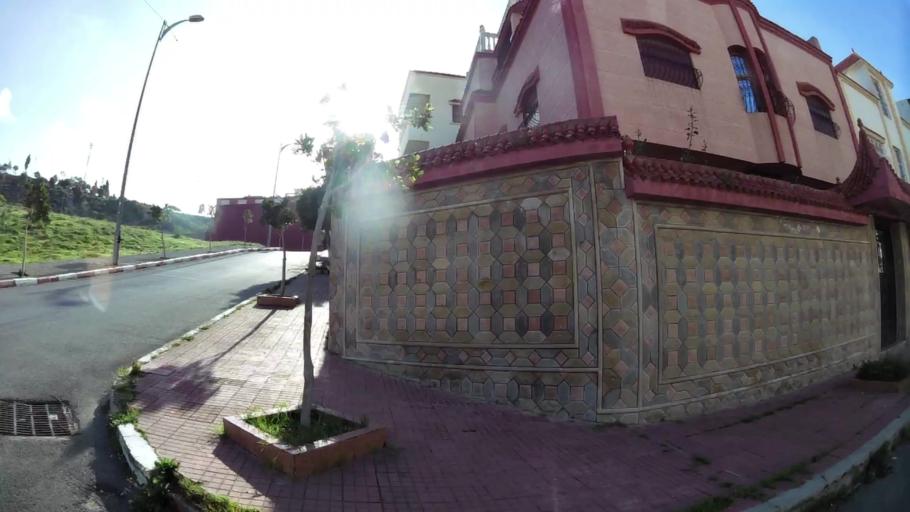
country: MA
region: Tanger-Tetouan
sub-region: Tanger-Assilah
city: Tangier
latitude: 35.7652
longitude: -5.7933
